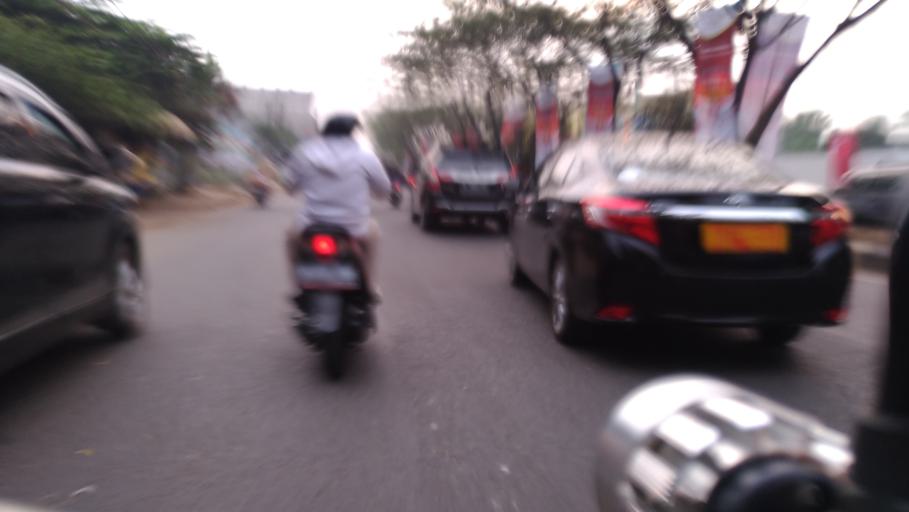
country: ID
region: West Java
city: Cileungsir
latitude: -6.3761
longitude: 106.9018
